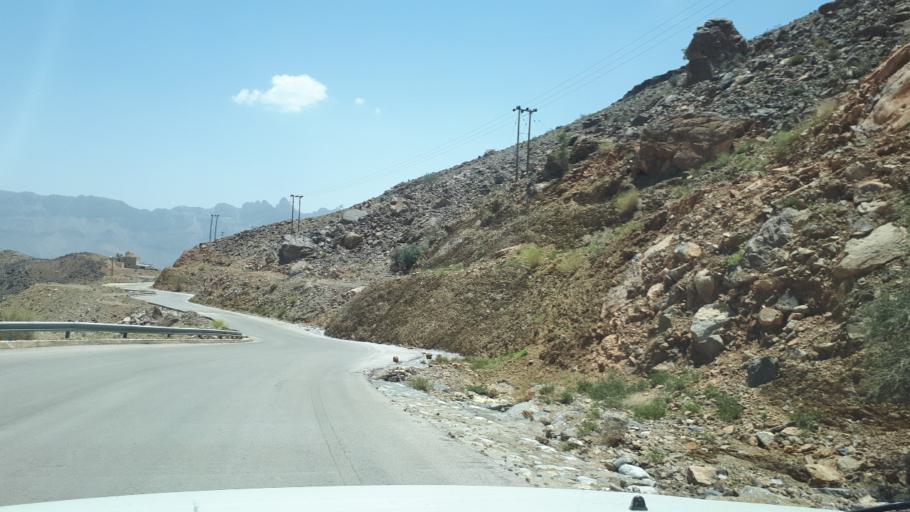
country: OM
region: Muhafazat ad Dakhiliyah
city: Bahla'
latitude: 23.2195
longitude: 57.1457
